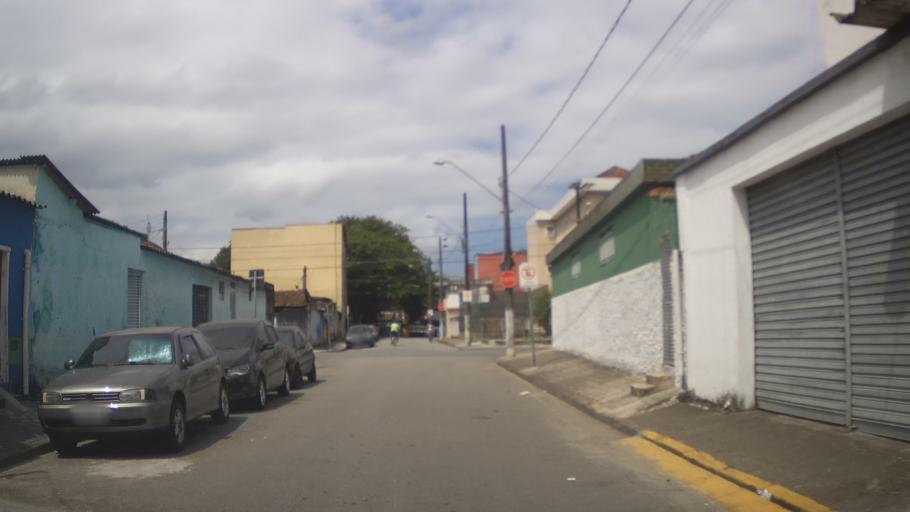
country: BR
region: Sao Paulo
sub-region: Santos
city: Santos
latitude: -23.9622
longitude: -46.3090
